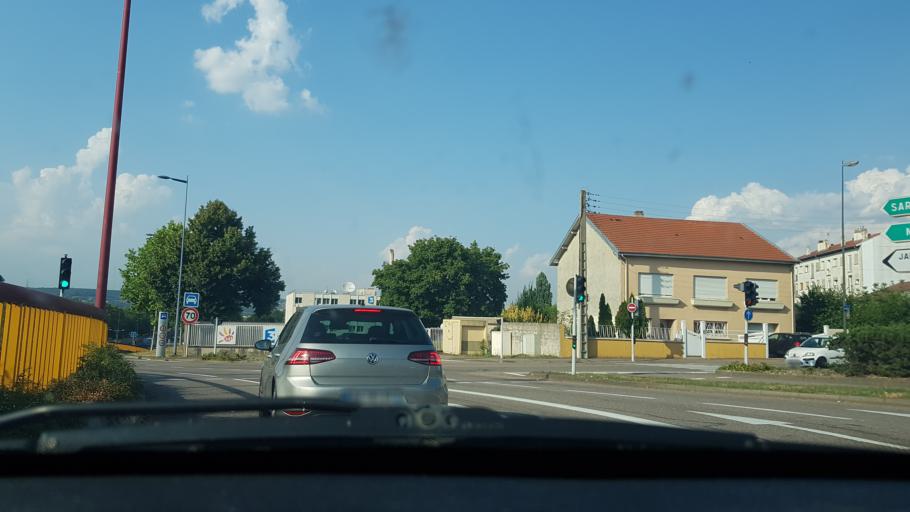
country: FR
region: Lorraine
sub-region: Departement de Meurthe-et-Moselle
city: Jarville-la-Malgrange
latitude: 48.6672
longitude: 6.1913
